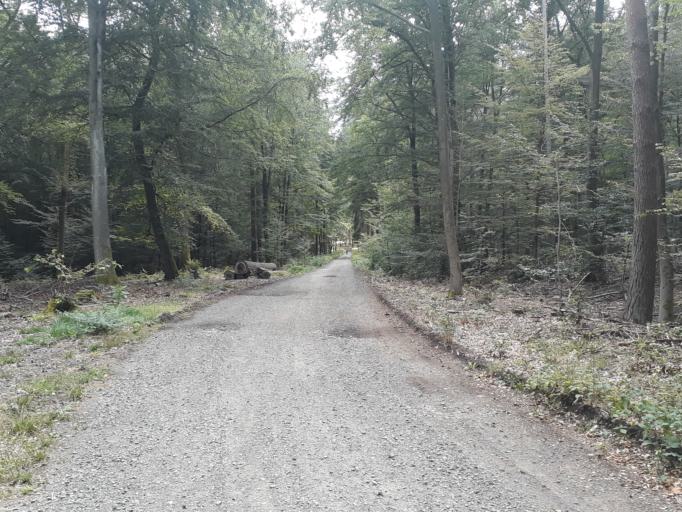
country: DE
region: Rheinland-Pfalz
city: Kaiserslautern
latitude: 49.4263
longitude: 7.7879
